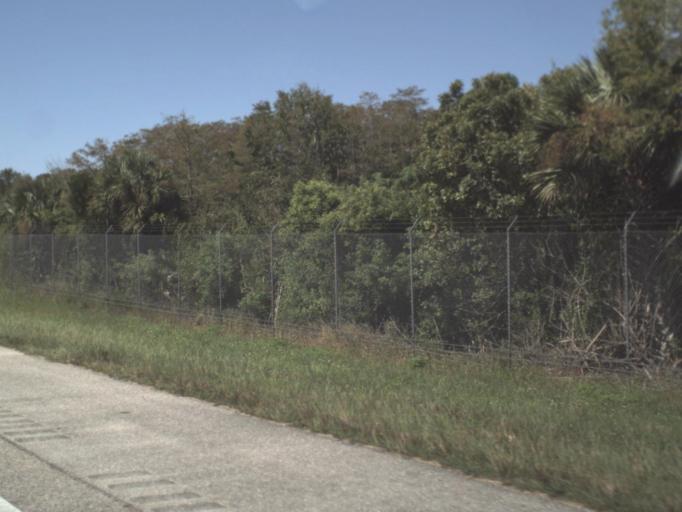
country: US
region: Florida
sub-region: Collier County
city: Orangetree
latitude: 26.1536
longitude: -81.4500
